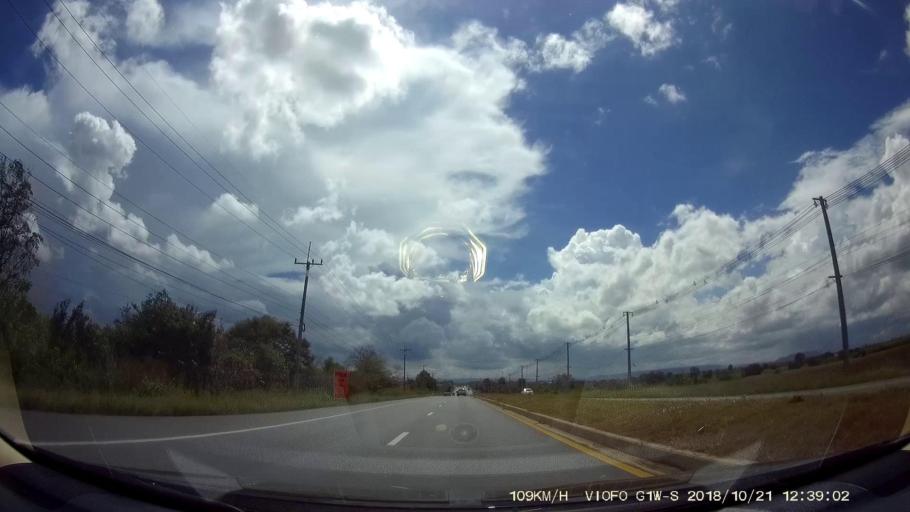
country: TH
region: Nakhon Ratchasima
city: Amphoe Sikhiu
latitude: 15.0448
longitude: 101.7027
